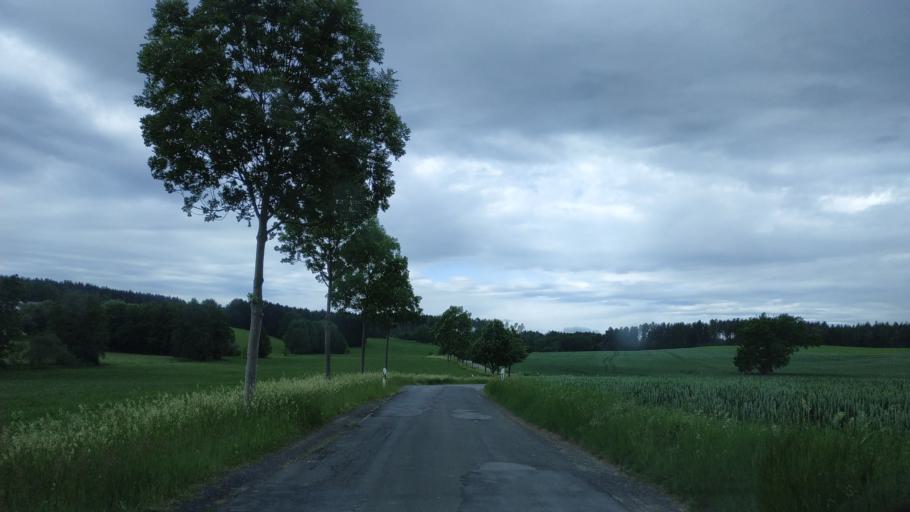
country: DE
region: Saxony
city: Plauen
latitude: 50.5423
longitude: 12.1314
